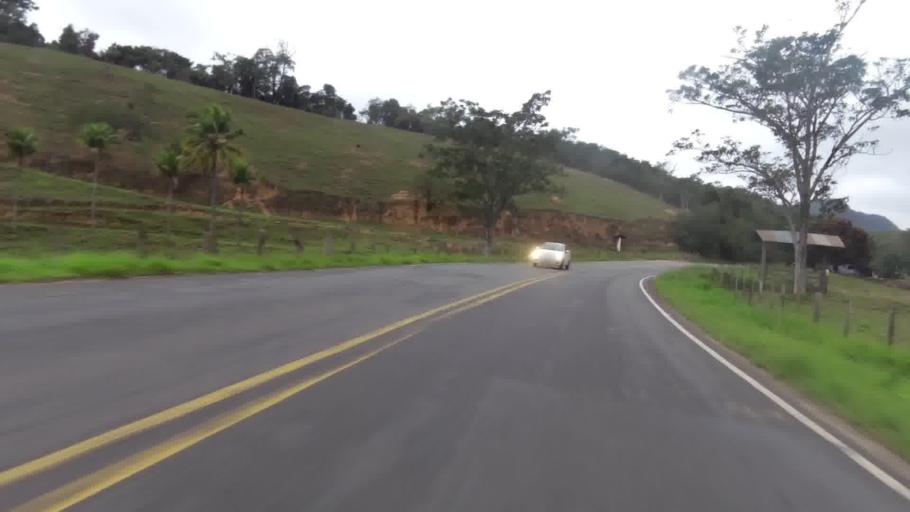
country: BR
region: Espirito Santo
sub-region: Alfredo Chaves
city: Alfredo Chaves
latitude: -20.6824
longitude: -40.7062
